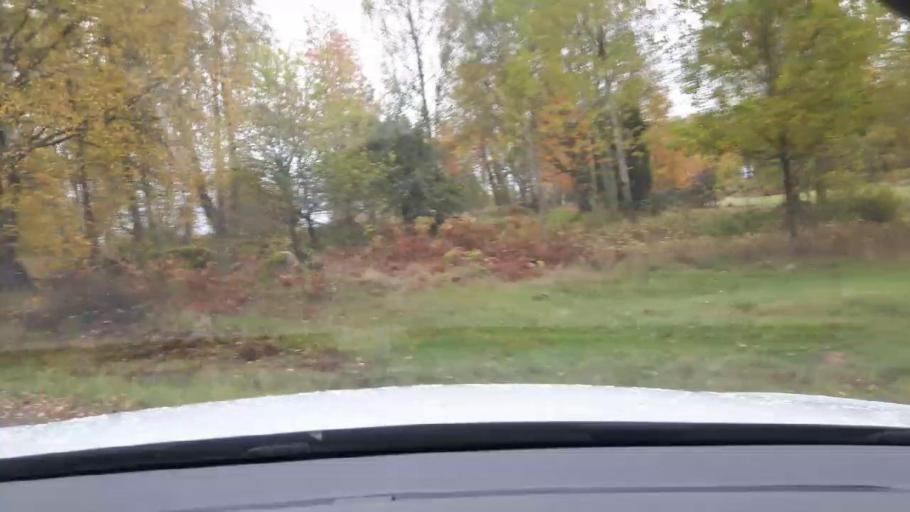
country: SE
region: Kalmar
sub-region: Vimmerby Kommun
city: Sodra Vi
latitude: 57.9585
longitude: 15.8987
